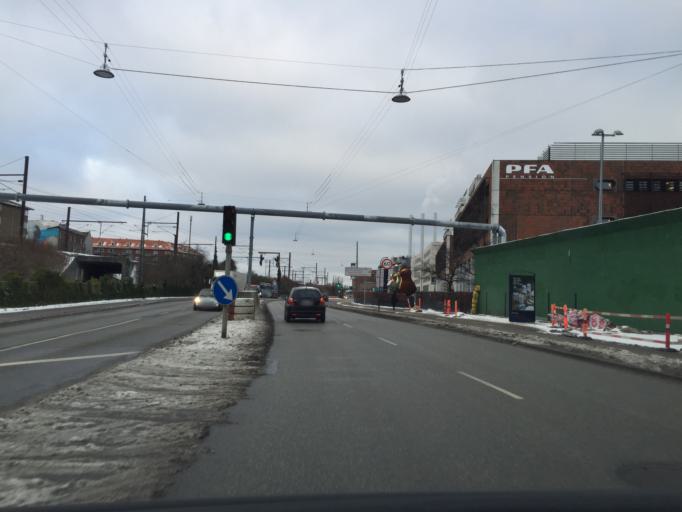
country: DK
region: Capital Region
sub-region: Kobenhavn
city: Christianshavn
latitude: 55.7073
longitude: 12.5910
